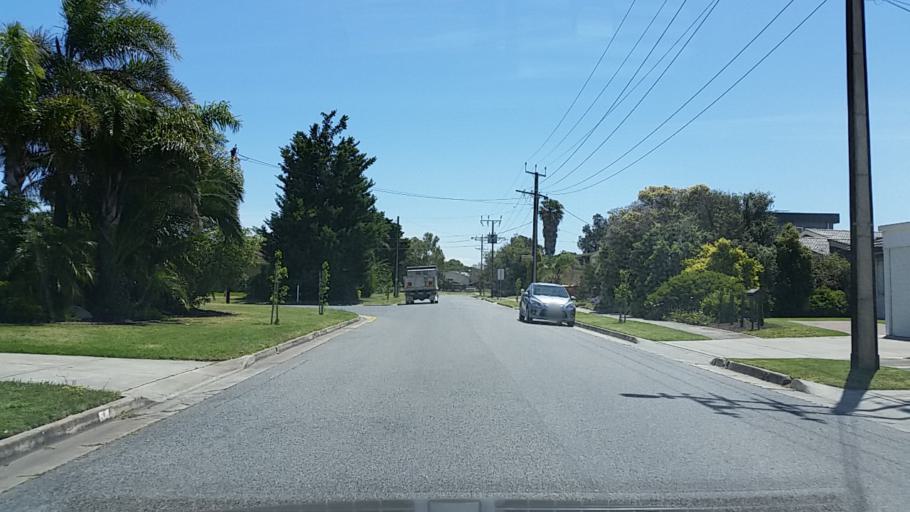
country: AU
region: South Australia
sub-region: Charles Sturt
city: Grange
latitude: -34.8912
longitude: 138.4997
